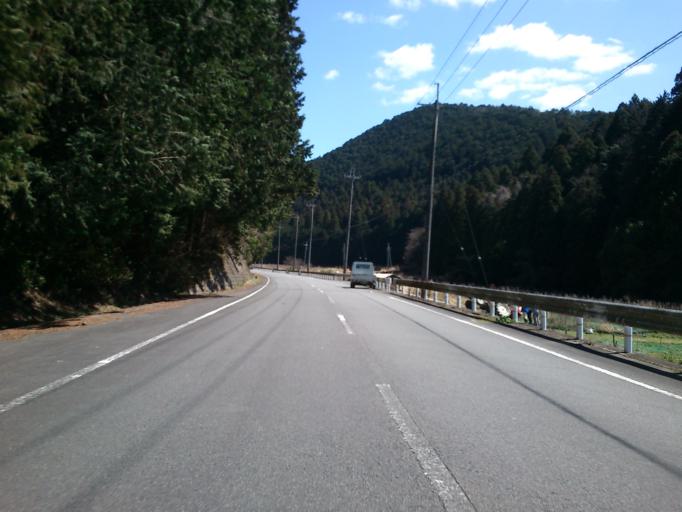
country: JP
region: Kyoto
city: Uji
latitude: 34.8317
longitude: 135.8720
